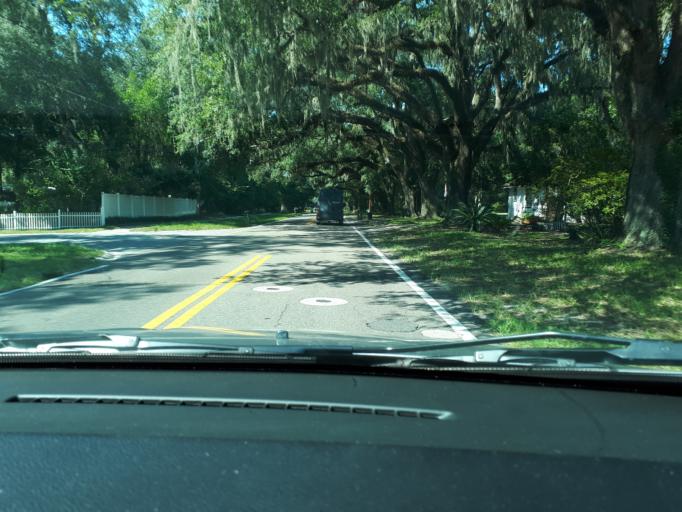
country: US
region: Florida
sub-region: Clay County
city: Bellair-Meadowbrook Terrace
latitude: 30.2770
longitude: -81.8318
